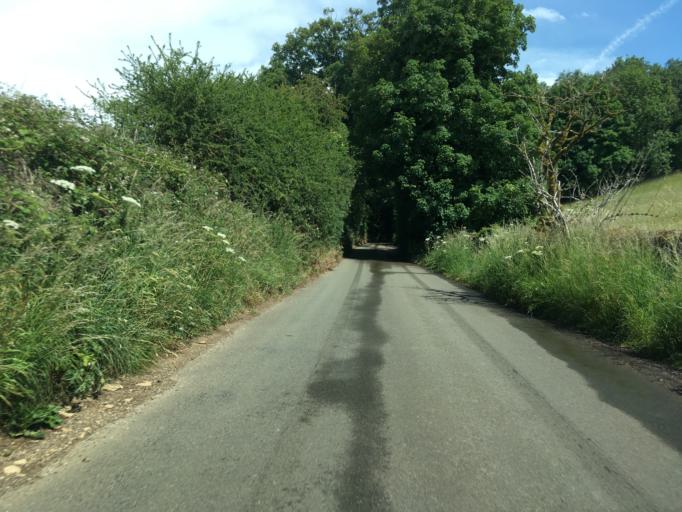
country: GB
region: England
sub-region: Gloucestershire
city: Tetbury
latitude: 51.6499
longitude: -2.1770
